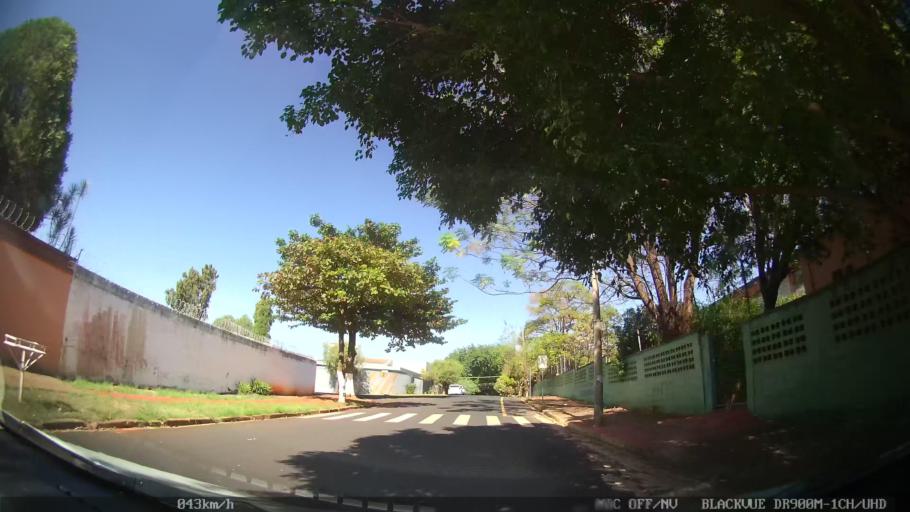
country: BR
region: Sao Paulo
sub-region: Ribeirao Preto
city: Ribeirao Preto
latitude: -21.2024
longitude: -47.7773
